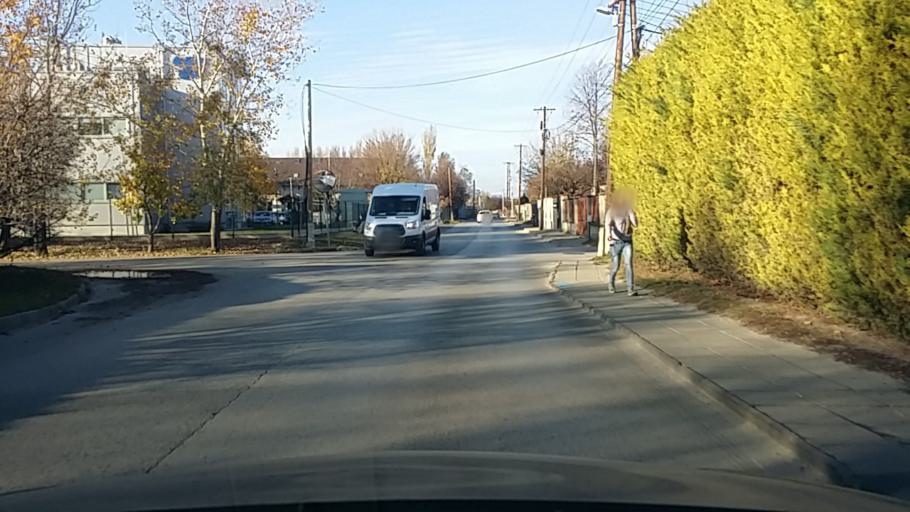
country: HU
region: Pest
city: Szigetszentmiklos
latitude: 47.3407
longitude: 19.0284
